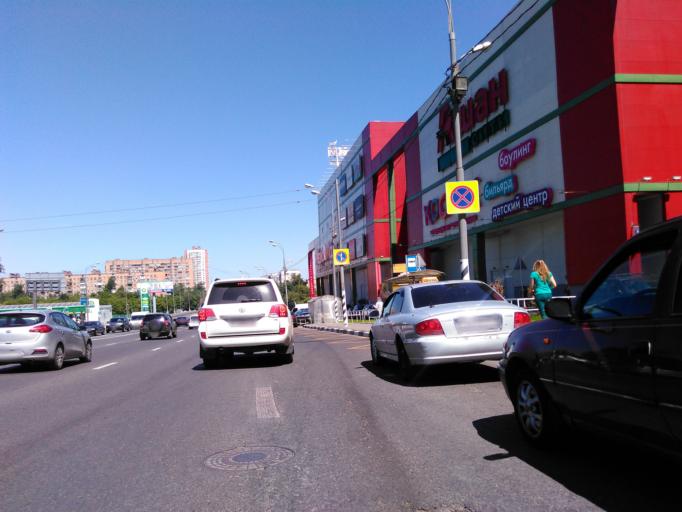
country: RU
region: Moscow
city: Novyye Cheremushki
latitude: 55.6876
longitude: 37.6035
